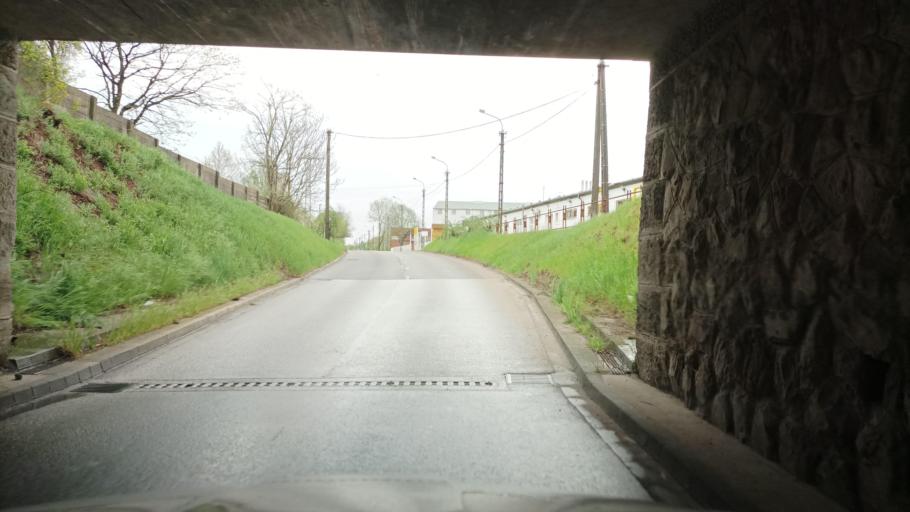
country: HU
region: Pest
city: Nagykoros
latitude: 47.0355
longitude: 19.7587
